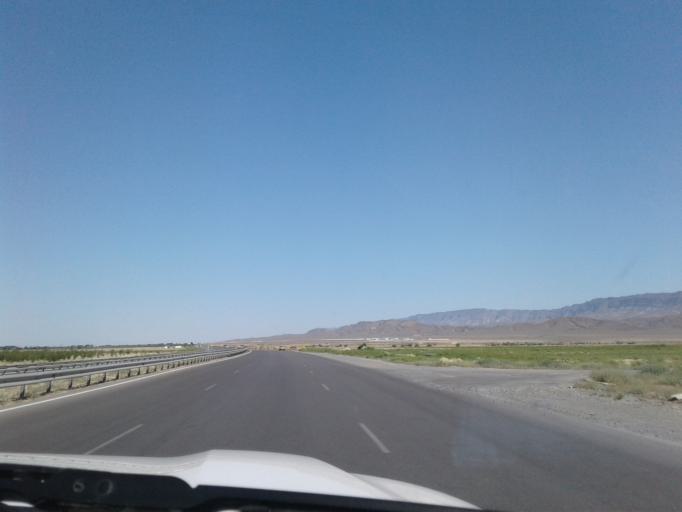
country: TM
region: Ahal
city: Annau
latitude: 37.8118
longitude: 58.7784
